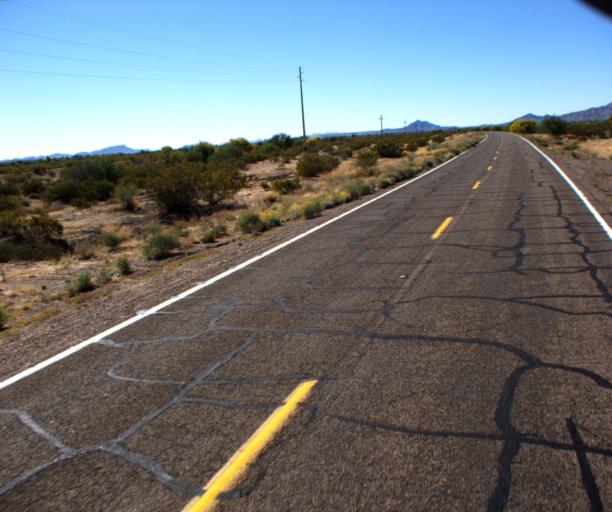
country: US
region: Arizona
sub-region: Pima County
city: Ajo
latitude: 32.4936
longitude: -112.8818
